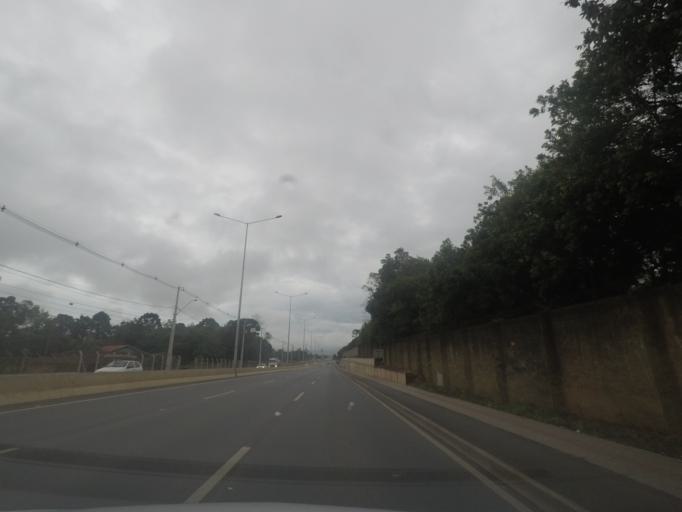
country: BR
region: Parana
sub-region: Piraquara
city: Piraquara
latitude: -25.4544
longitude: -49.1122
